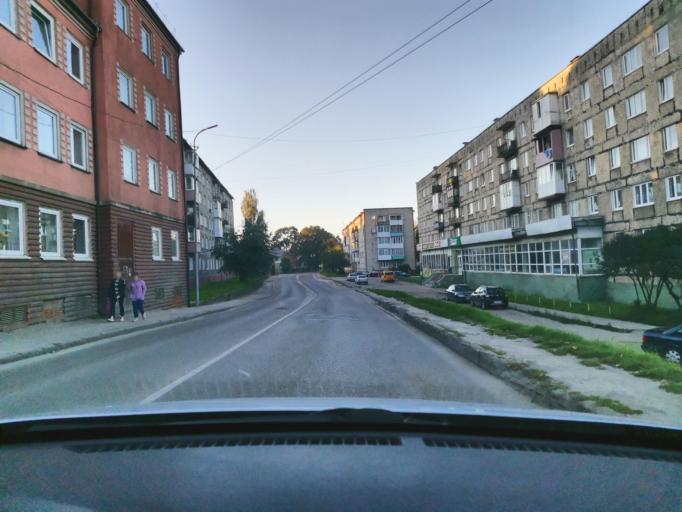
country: RU
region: Kaliningrad
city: Chernyakhovsk
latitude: 54.6398
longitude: 21.8076
